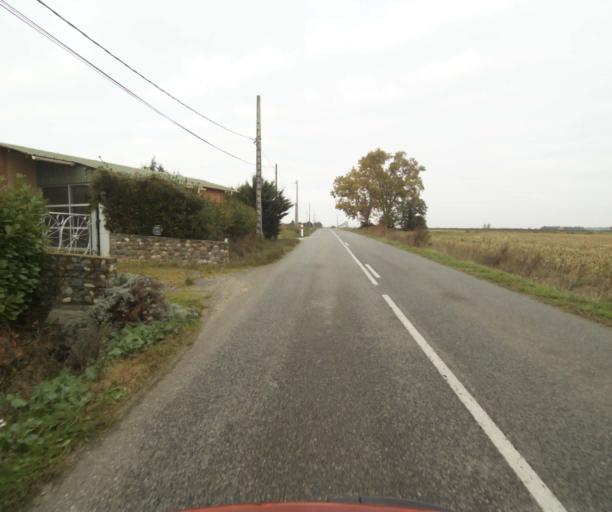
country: FR
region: Midi-Pyrenees
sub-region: Departement du Tarn-et-Garonne
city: Verdun-sur-Garonne
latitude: 43.8087
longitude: 1.2047
